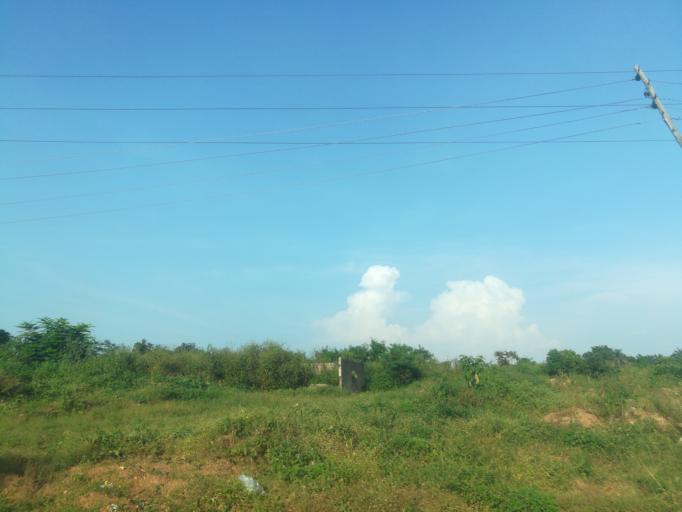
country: NG
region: Oyo
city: Moniya
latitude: 7.5508
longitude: 3.8914
